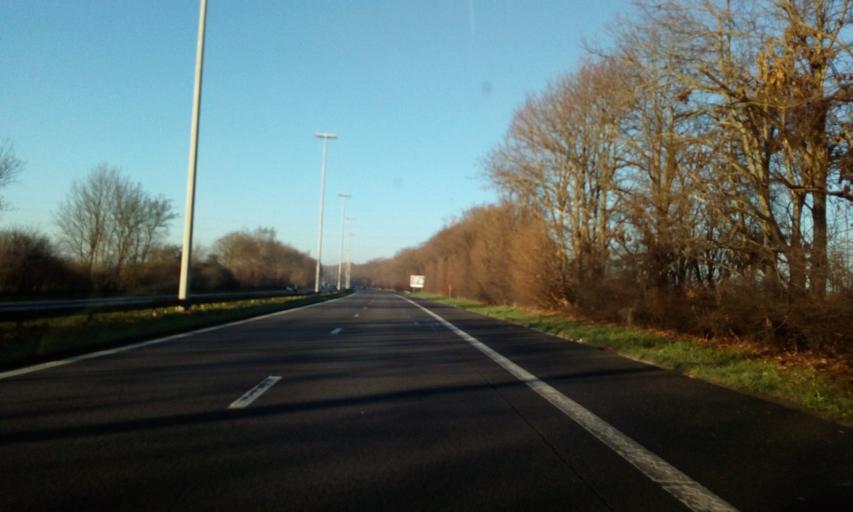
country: BE
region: Wallonia
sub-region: Province du Hainaut
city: Pont-a-Celles
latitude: 50.5481
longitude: 4.3703
